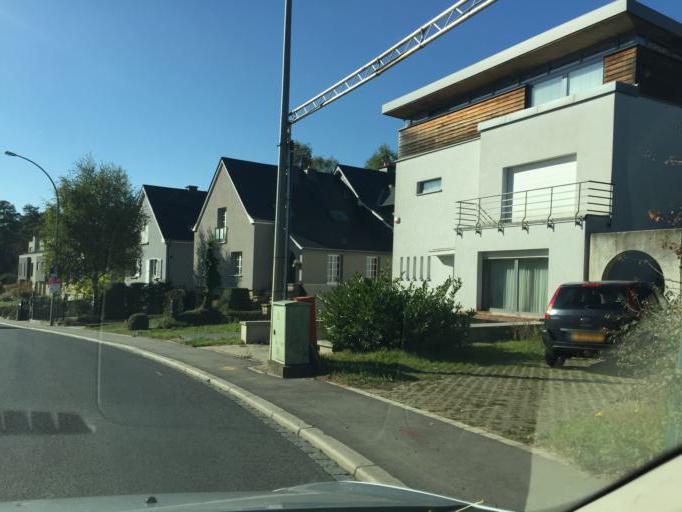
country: LU
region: Luxembourg
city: Bridel
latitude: 49.6602
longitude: 6.0804
